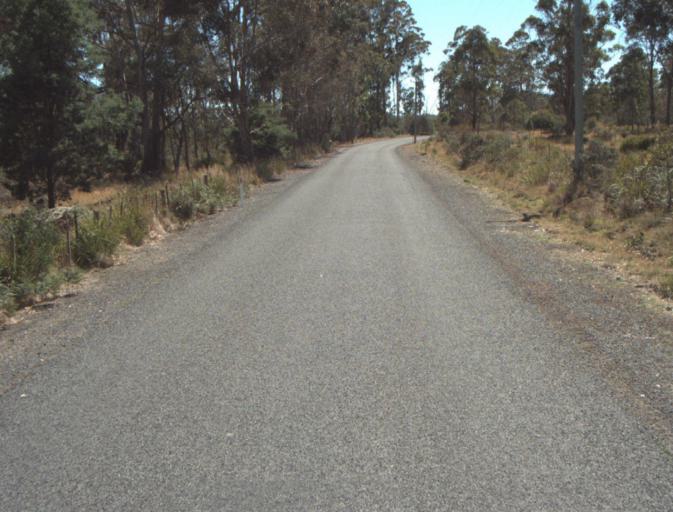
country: AU
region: Tasmania
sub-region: Launceston
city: Newstead
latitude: -41.3724
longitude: 147.2977
